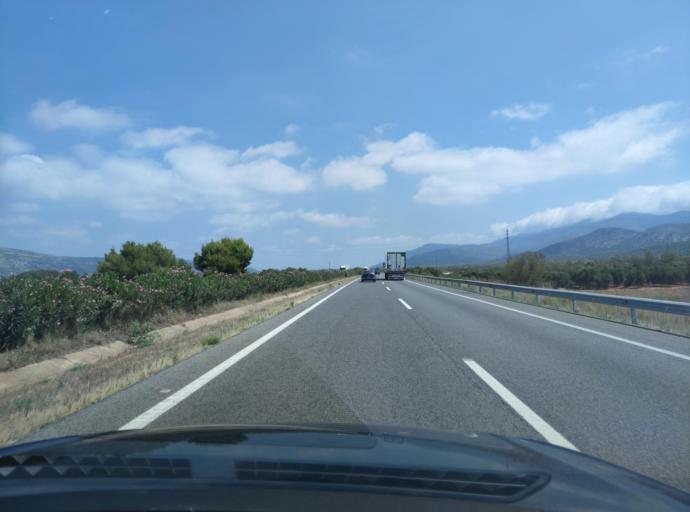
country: ES
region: Catalonia
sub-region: Provincia de Tarragona
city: Ulldecona
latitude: 40.5847
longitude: 0.4577
